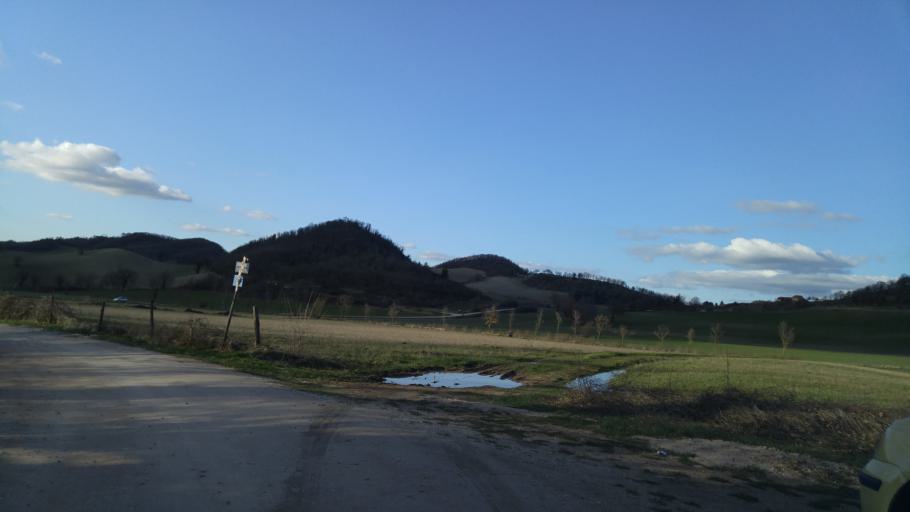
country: IT
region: The Marches
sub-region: Provincia di Pesaro e Urbino
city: Cagli
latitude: 43.5411
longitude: 12.6814
